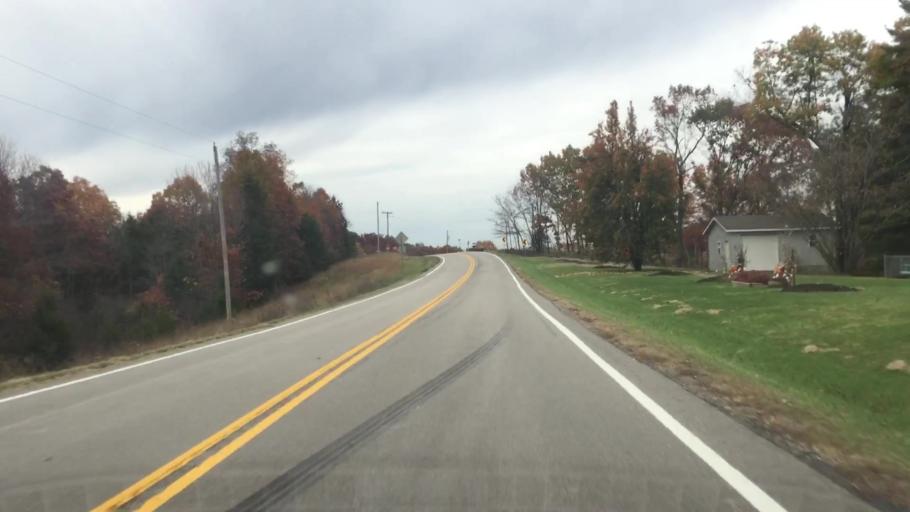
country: US
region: Missouri
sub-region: Gasconade County
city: Hermann
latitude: 38.7167
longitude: -91.6416
